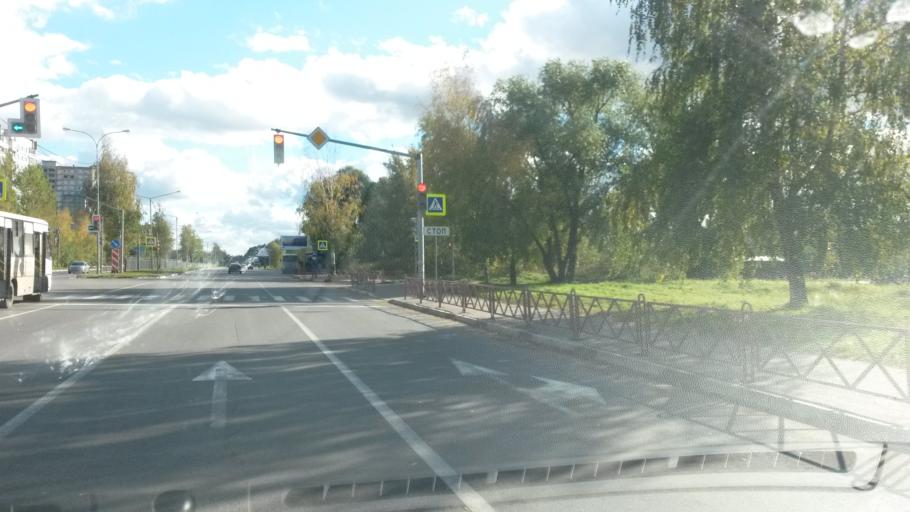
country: RU
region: Jaroslavl
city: Yaroslavl
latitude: 57.5685
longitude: 39.9262
